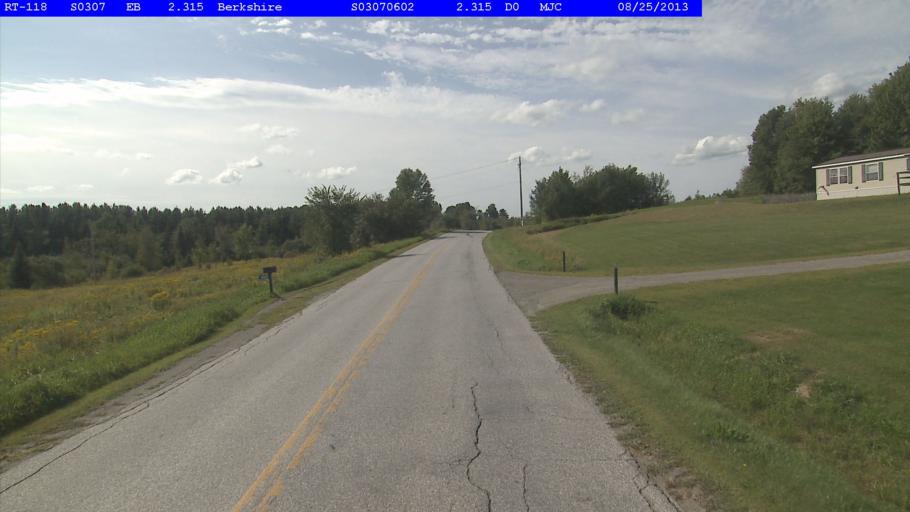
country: US
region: Vermont
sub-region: Franklin County
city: Enosburg Falls
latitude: 44.9509
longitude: -72.7485
